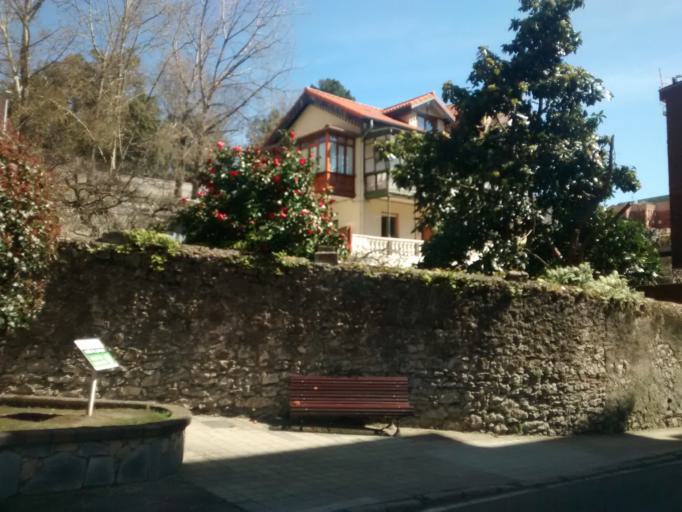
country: ES
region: Cantabria
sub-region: Provincia de Cantabria
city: Santander
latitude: 43.4664
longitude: -3.8128
